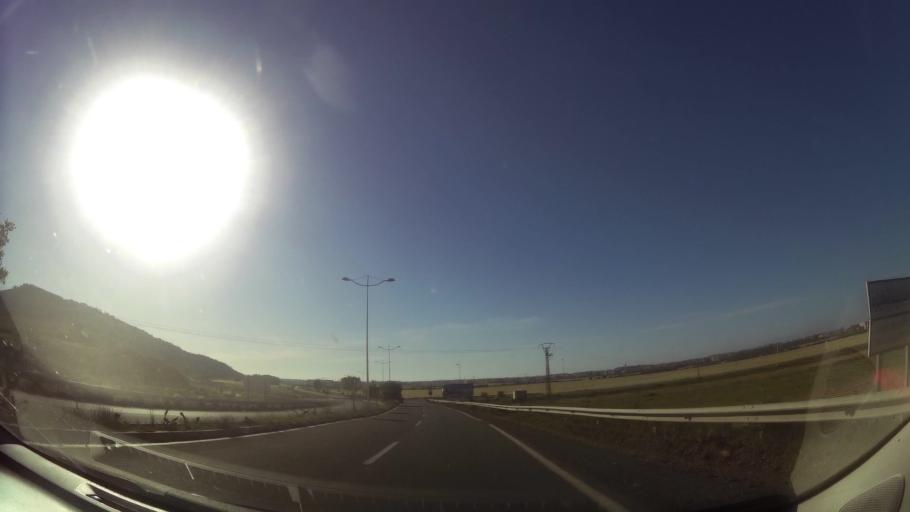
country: MA
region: Oriental
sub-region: Berkane-Taourirt
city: Madagh
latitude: 35.0633
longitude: -2.2252
